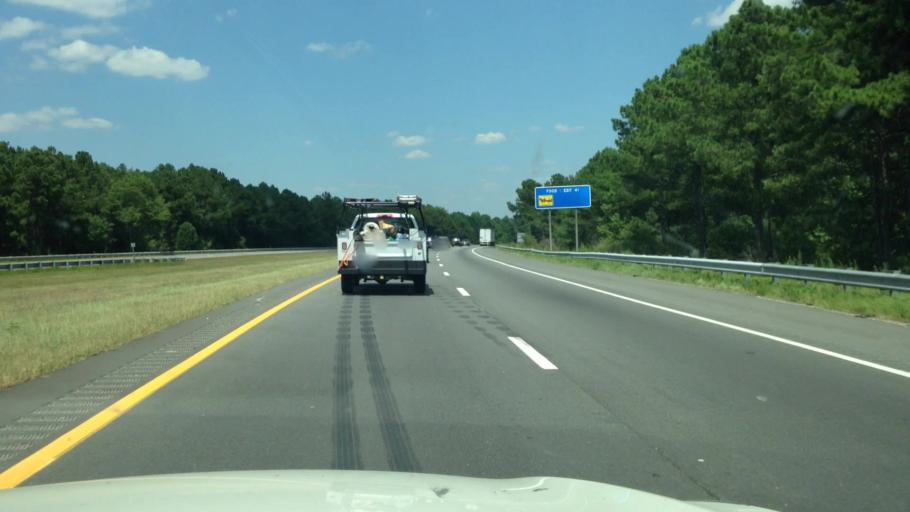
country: US
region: North Carolina
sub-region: Cumberland County
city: Hope Mills
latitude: 34.9316
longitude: -78.9376
